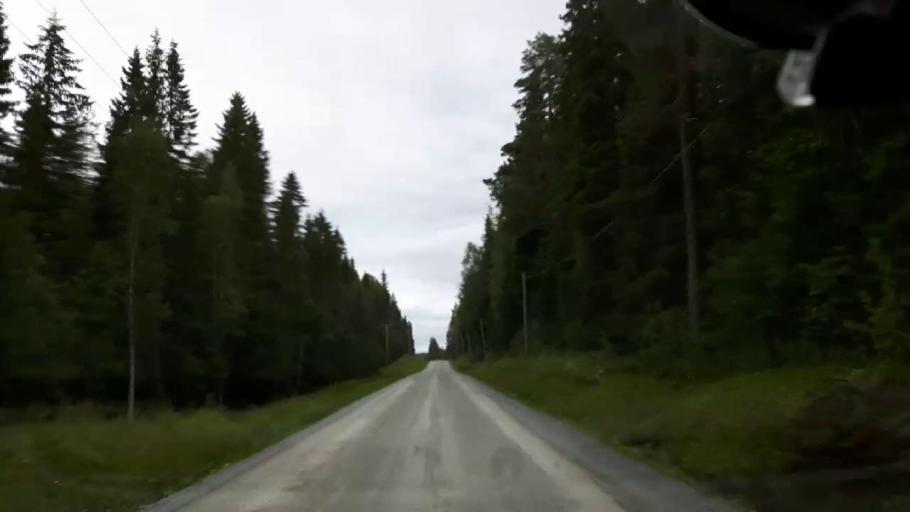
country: SE
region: Jaemtland
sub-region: Braecke Kommun
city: Braecke
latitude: 63.0767
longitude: 15.2918
